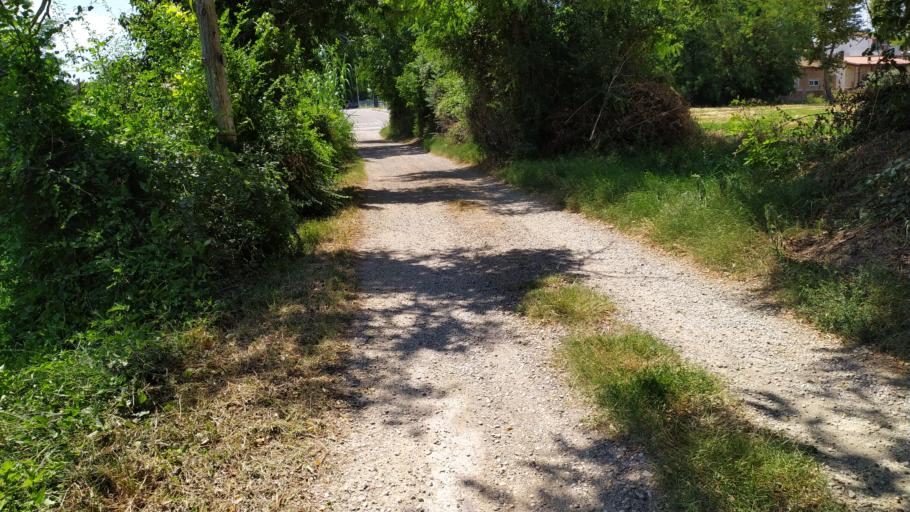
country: IT
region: Emilia-Romagna
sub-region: Forli-Cesena
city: Castrocaro Terme e Terra del Sole
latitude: 44.1873
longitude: 11.9642
